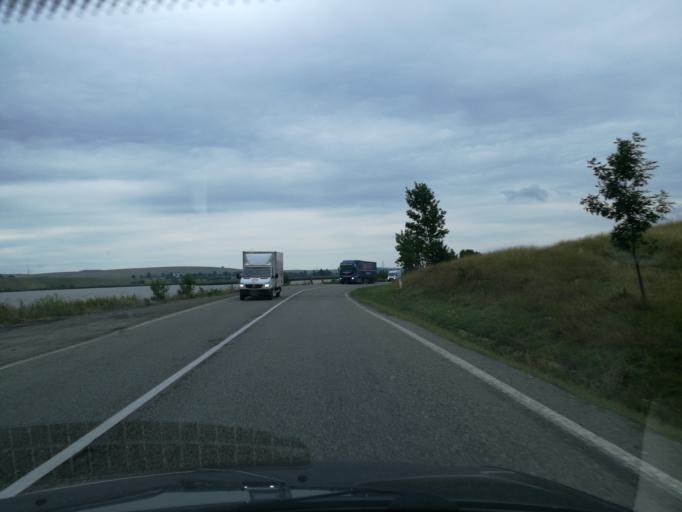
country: RO
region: Suceava
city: Bunesti-Regat
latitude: 47.4938
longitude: 26.2833
